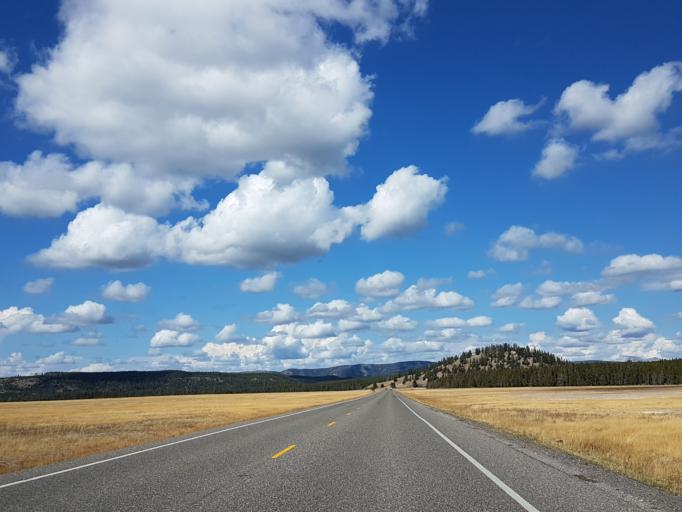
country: US
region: Montana
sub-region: Gallatin County
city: West Yellowstone
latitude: 44.5598
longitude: -110.8099
